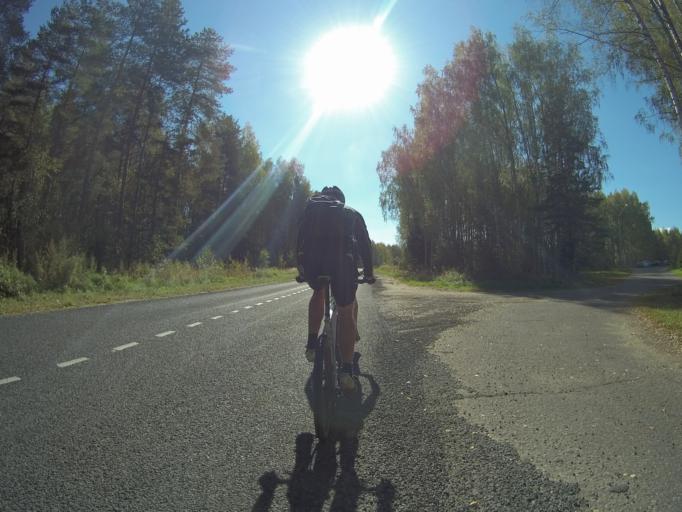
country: RU
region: Vladimir
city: Raduzhnyy
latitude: 55.9955
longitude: 40.2716
